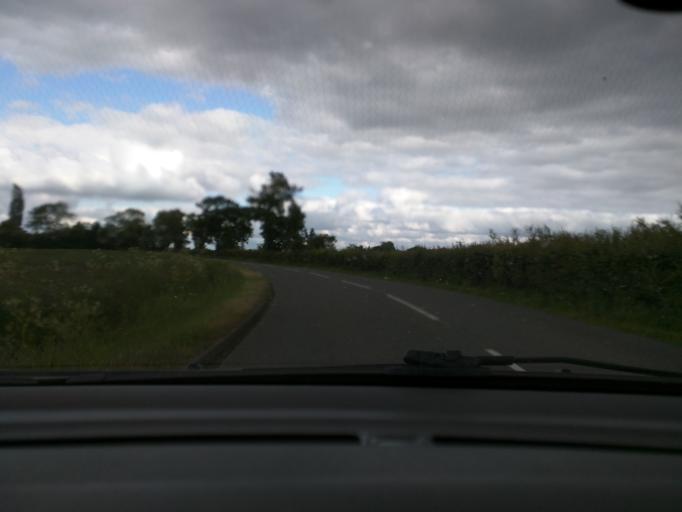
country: GB
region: England
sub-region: Suffolk
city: Framlingham
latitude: 52.2229
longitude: 1.3868
